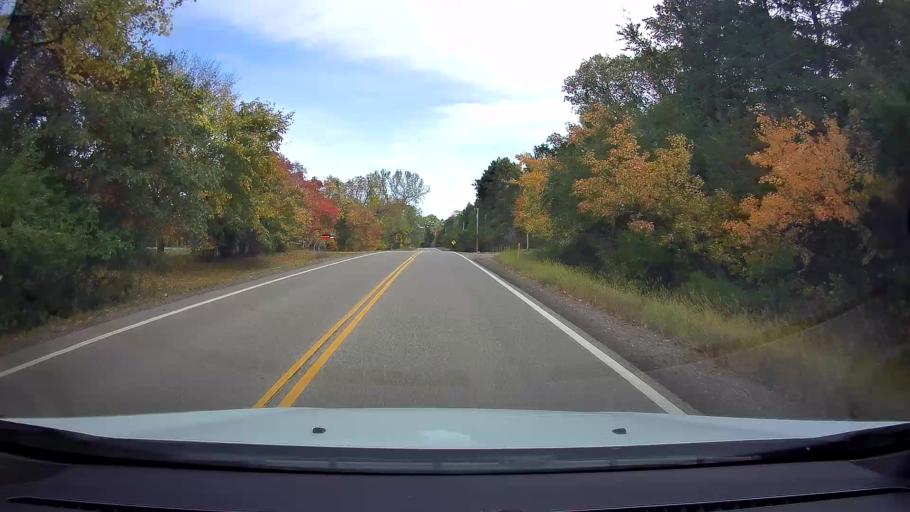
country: US
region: Minnesota
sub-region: Washington County
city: Stillwater
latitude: 45.0798
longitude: -92.8270
